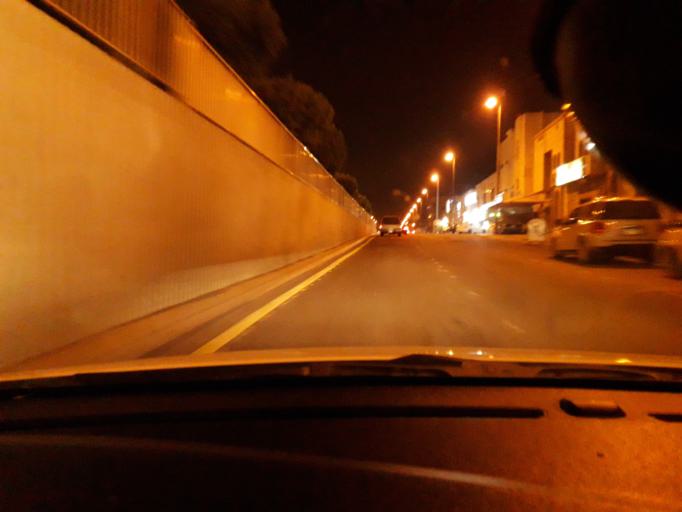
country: SA
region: Al Madinah al Munawwarah
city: Sultanah
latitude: 24.4713
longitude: 39.5560
